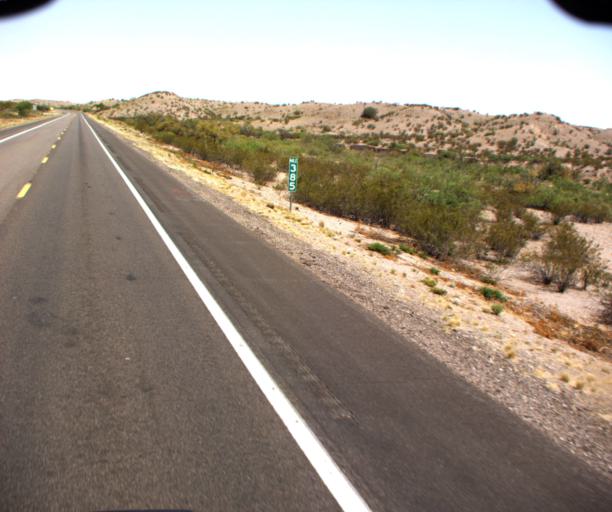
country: US
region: New Mexico
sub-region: Hidalgo County
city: Lordsburg
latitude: 32.6494
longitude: -109.0518
